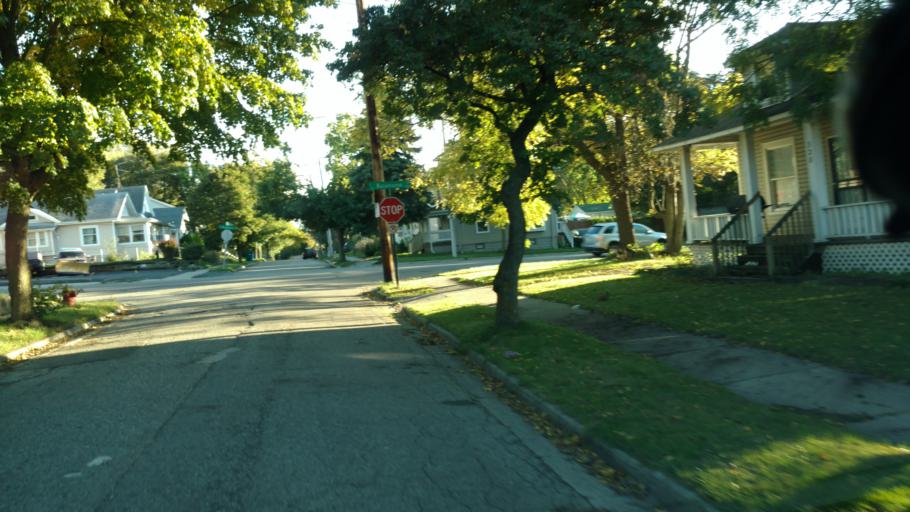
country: US
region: Michigan
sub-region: Ingham County
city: Lansing
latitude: 42.7302
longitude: -84.5297
